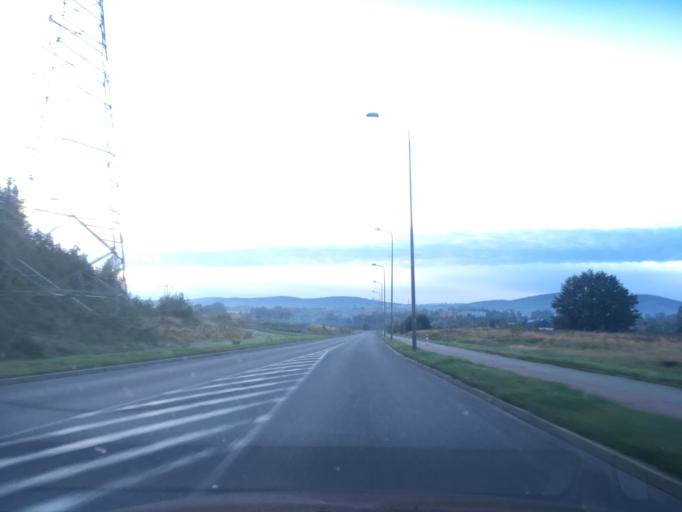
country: PL
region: Lower Silesian Voivodeship
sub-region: Powiat zgorzelecki
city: Bogatynia
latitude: 50.9151
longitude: 14.9598
